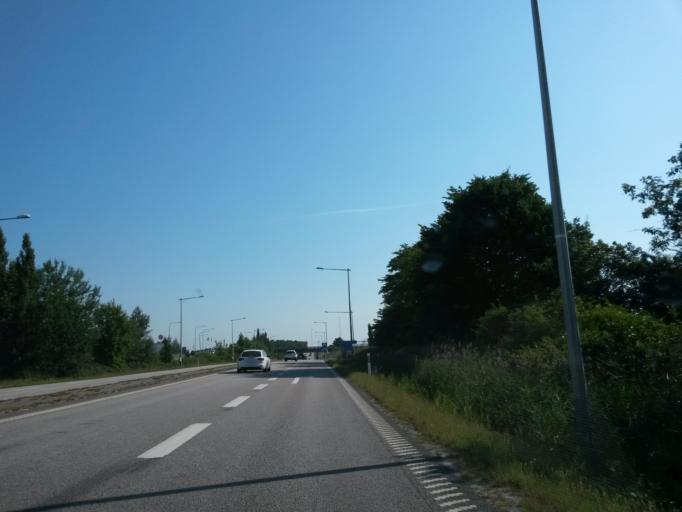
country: SE
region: Vaestra Goetaland
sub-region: Vara Kommun
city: Vara
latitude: 58.2550
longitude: 12.9675
